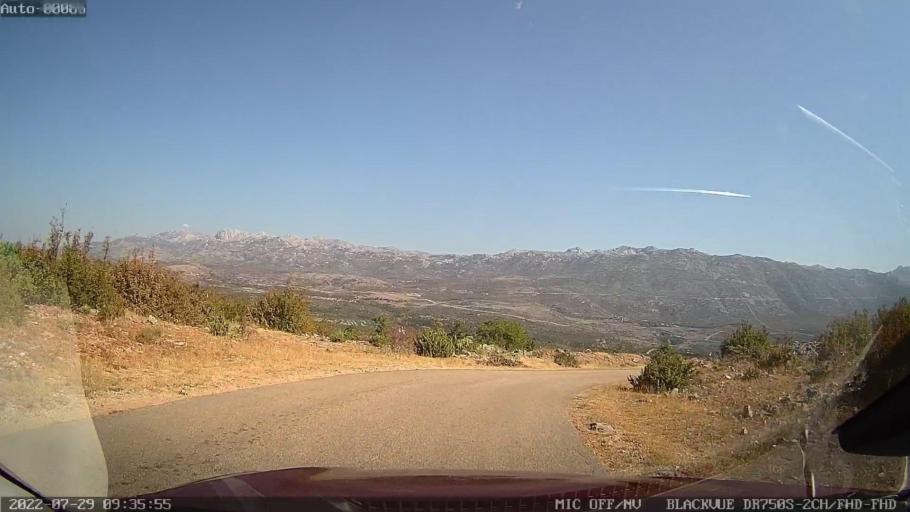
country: HR
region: Zadarska
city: Obrovac
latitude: 44.1885
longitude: 15.7331
